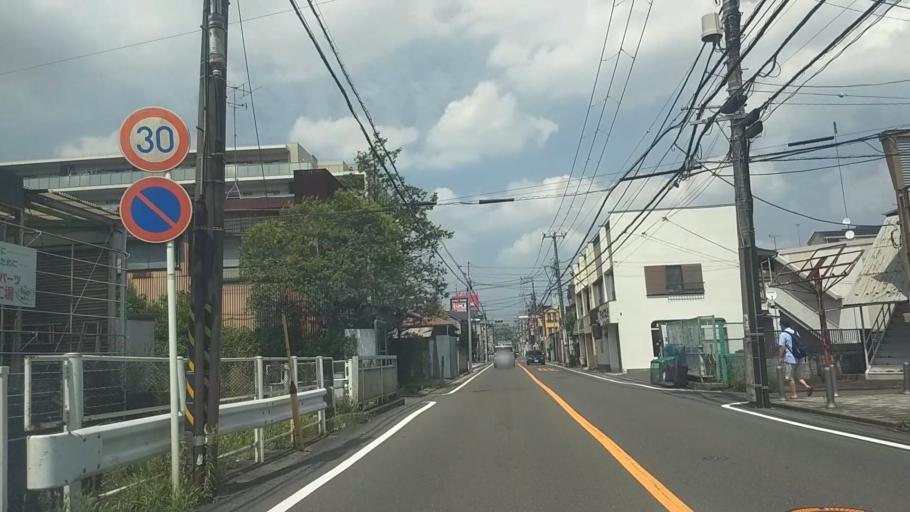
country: JP
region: Kanagawa
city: Yokohama
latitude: 35.4996
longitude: 139.6455
